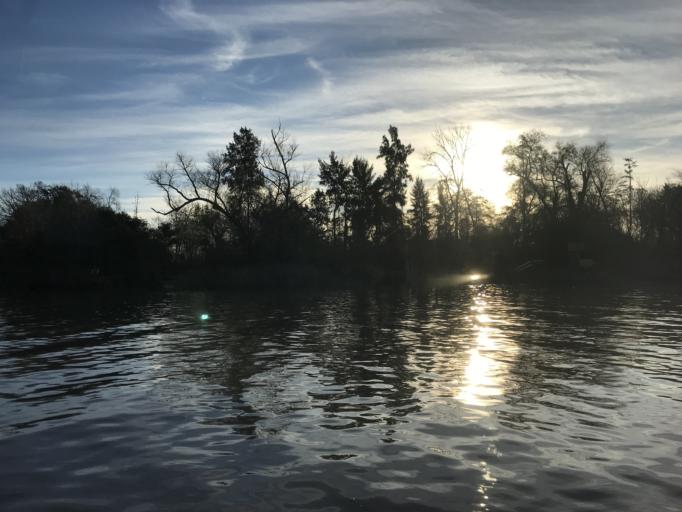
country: AR
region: Buenos Aires
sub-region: Partido de Tigre
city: Tigre
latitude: -34.3847
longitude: -58.5772
